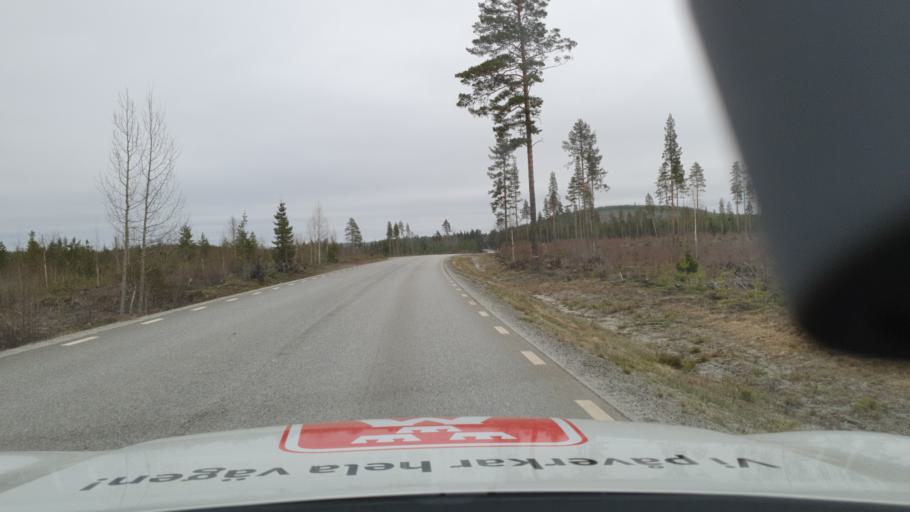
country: SE
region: Vaesterbotten
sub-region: Lycksele Kommun
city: Lycksele
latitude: 64.6443
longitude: 18.5049
